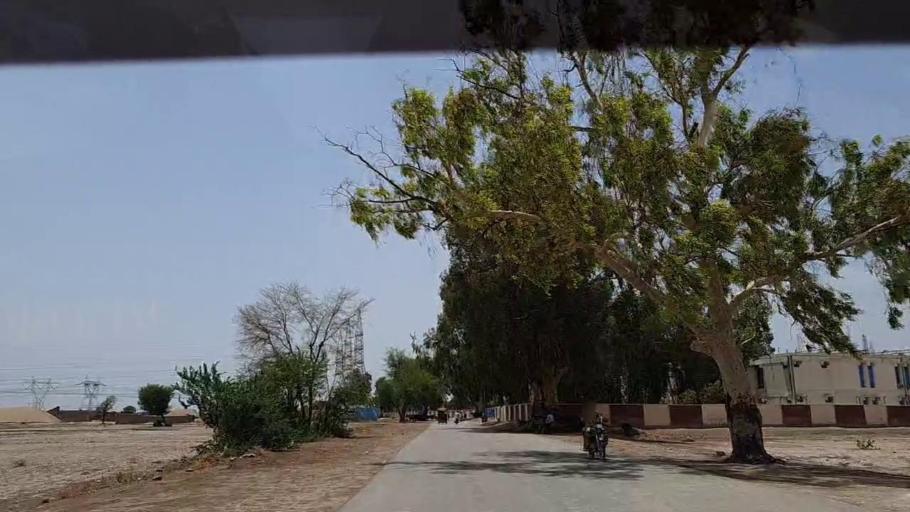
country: PK
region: Sindh
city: Dadu
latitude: 26.7170
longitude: 67.7467
